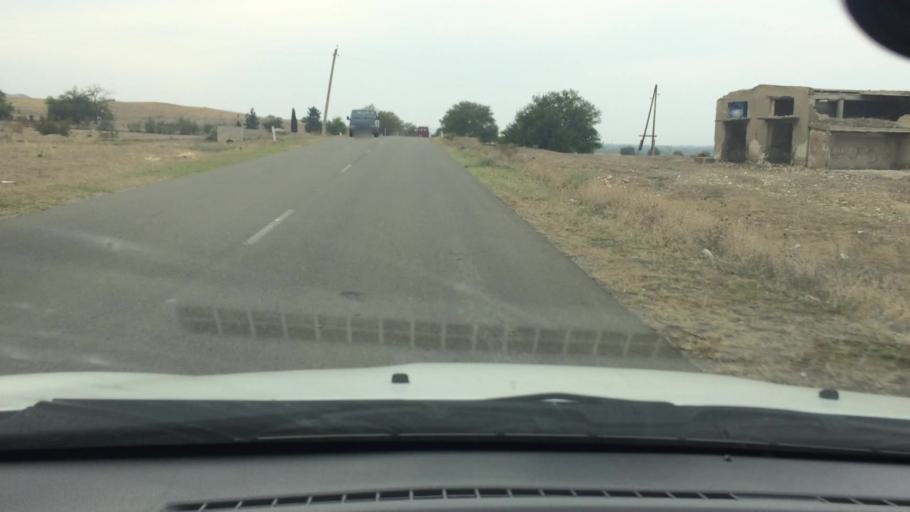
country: AM
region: Tavush
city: Berdavan
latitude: 41.3371
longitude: 45.0134
